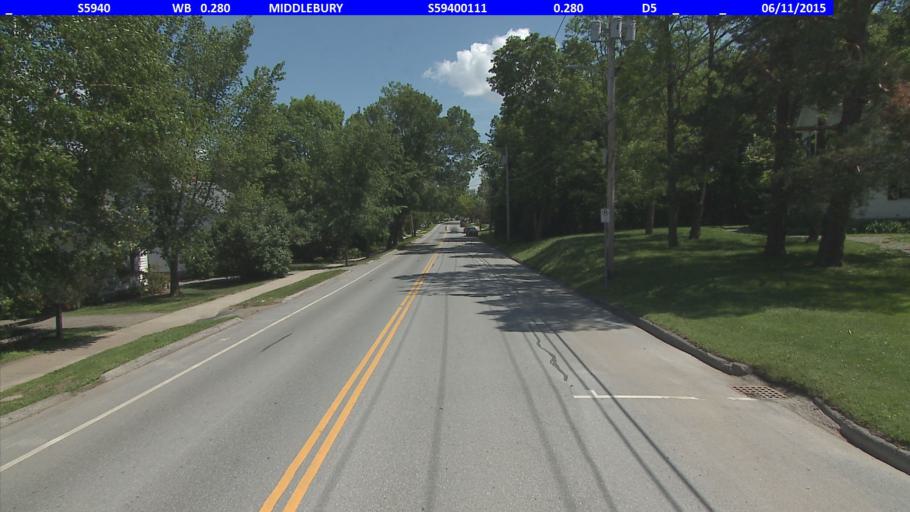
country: US
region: Vermont
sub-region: Addison County
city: Middlebury (village)
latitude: 44.0145
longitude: -73.1751
